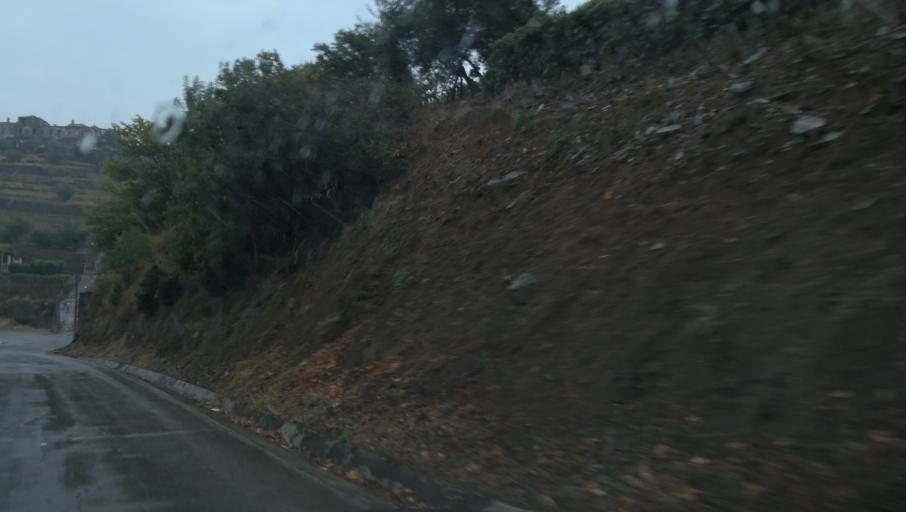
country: PT
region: Vila Real
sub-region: Peso da Regua
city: Peso da Regua
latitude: 41.1703
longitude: -7.7513
